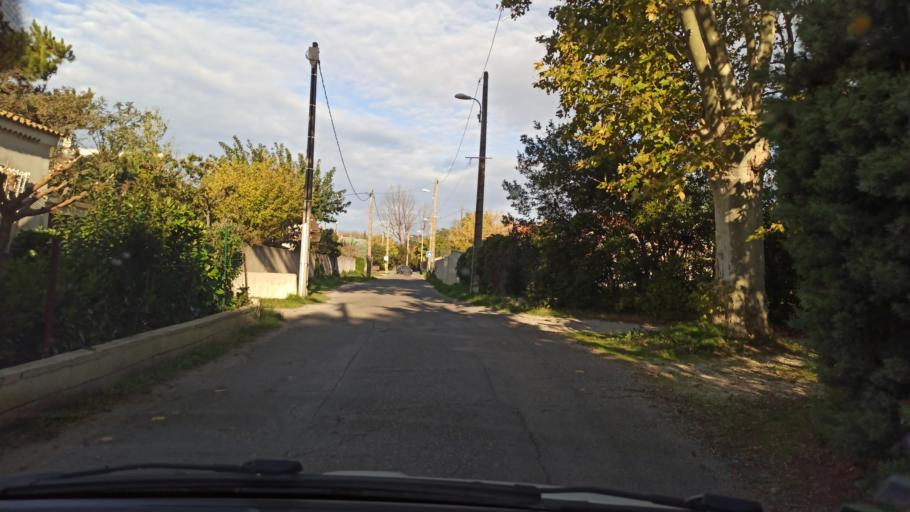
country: FR
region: Provence-Alpes-Cote d'Azur
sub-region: Departement du Vaucluse
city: Montfavet
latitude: 43.9340
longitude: 4.8836
